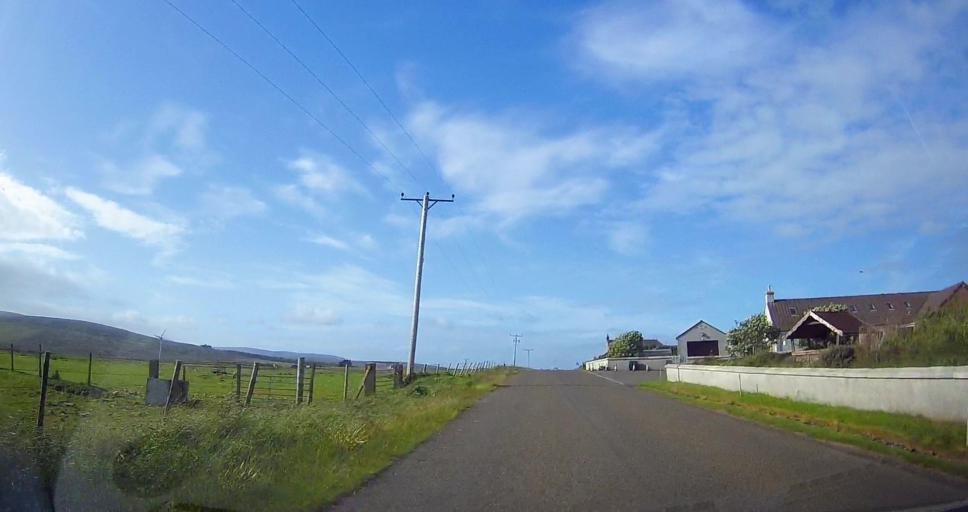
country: GB
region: Scotland
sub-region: Orkney Islands
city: Stromness
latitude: 58.8156
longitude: -3.2024
